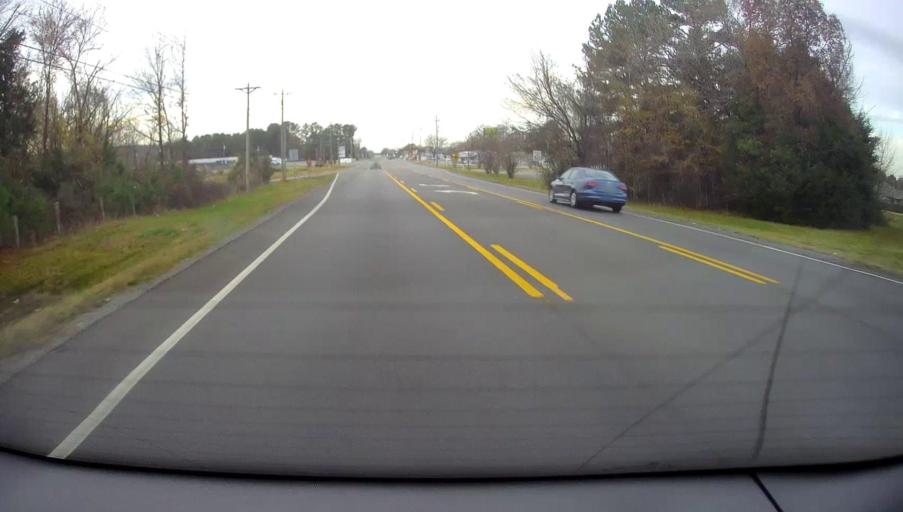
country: US
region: Alabama
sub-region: Morgan County
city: Priceville
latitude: 34.5177
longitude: -86.8849
